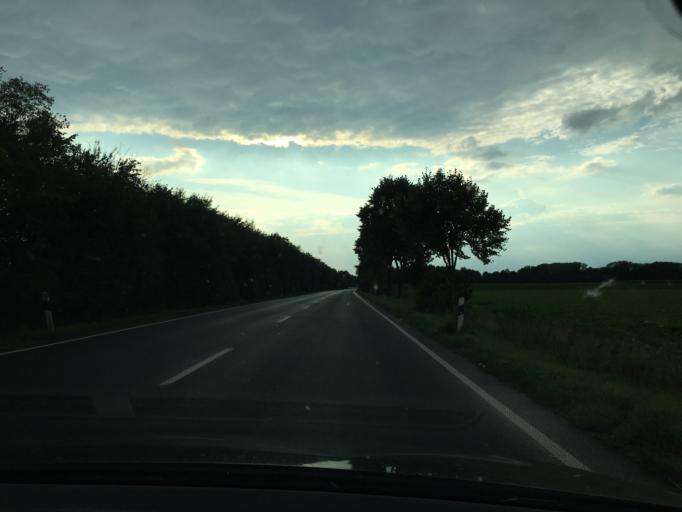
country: DE
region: North Rhine-Westphalia
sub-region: Regierungsbezirk Koln
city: Kerpen
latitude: 50.8236
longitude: 6.7048
